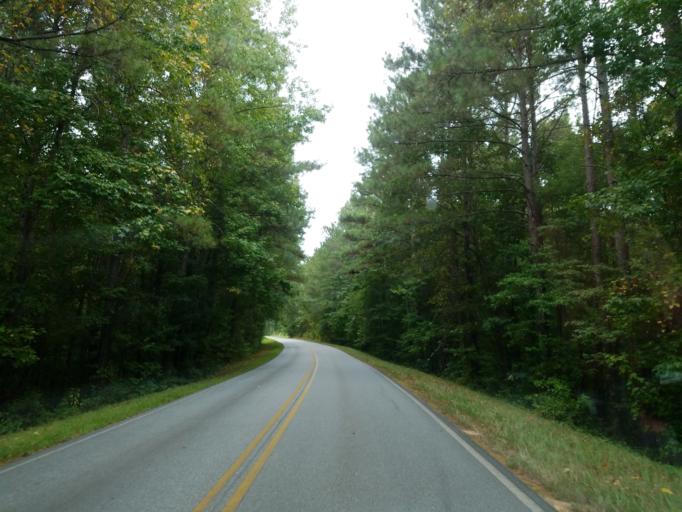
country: US
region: Georgia
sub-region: Monroe County
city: Forsyth
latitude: 32.9118
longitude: -83.9097
